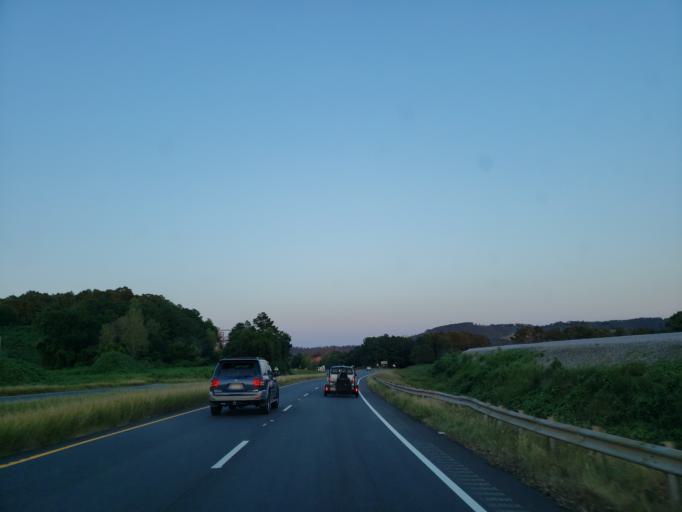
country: US
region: Georgia
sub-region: Bartow County
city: Cartersville
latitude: 34.1547
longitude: -84.7772
